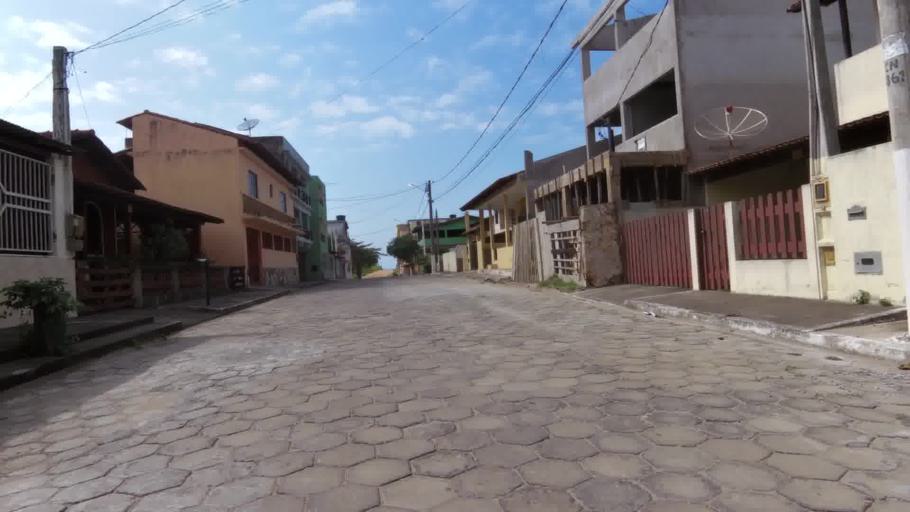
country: BR
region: Espirito Santo
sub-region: Marataizes
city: Marataizes
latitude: -21.0335
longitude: -40.8150
